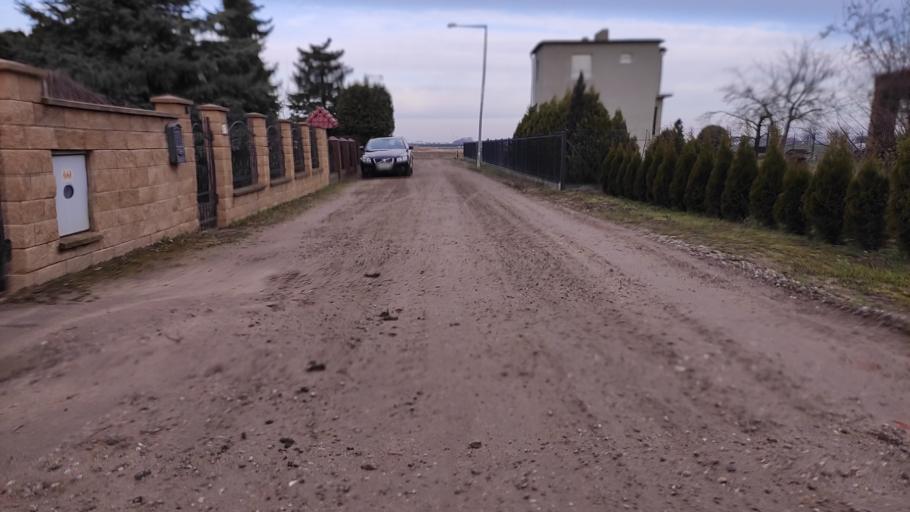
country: PL
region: Greater Poland Voivodeship
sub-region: Powiat poznanski
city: Swarzedz
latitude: 52.4008
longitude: 17.1520
